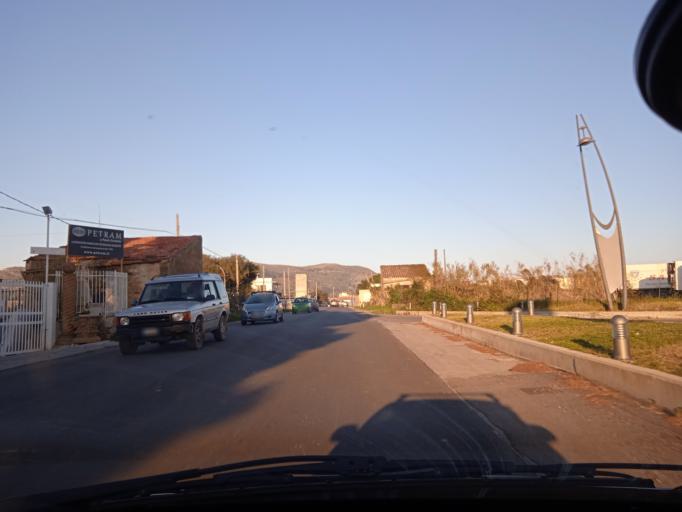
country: IT
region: Sicily
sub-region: Palermo
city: Ficarazzi
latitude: 38.0916
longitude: 13.4814
